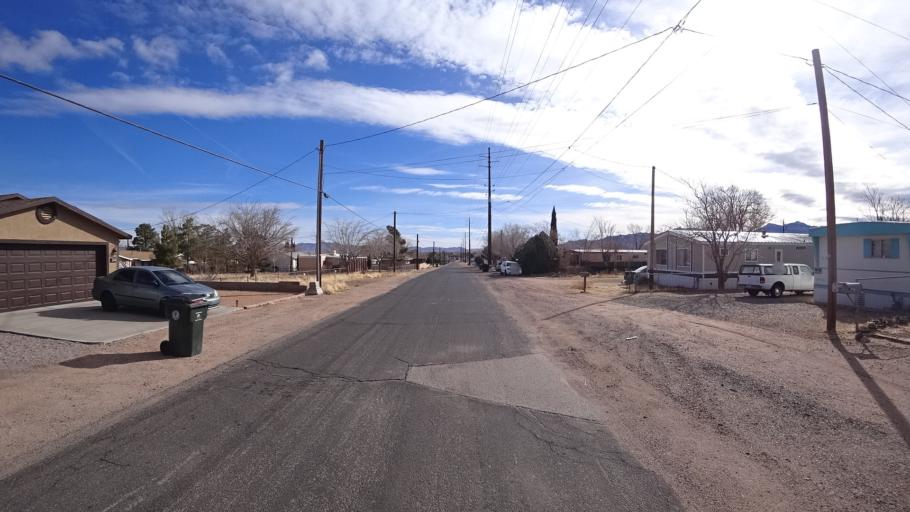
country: US
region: Arizona
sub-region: Mohave County
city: Kingman
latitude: 35.2171
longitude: -114.0503
